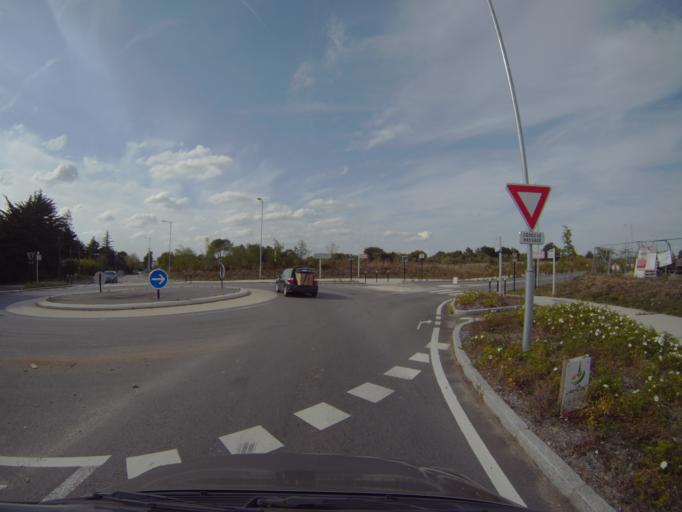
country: FR
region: Pays de la Loire
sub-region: Departement de la Loire-Atlantique
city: Sautron
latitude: 47.2447
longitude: -1.6850
